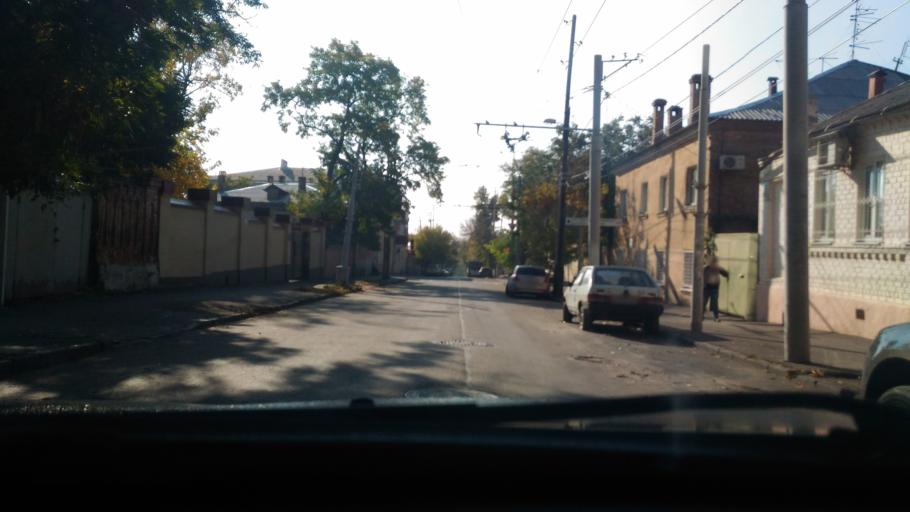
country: RU
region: Rostov
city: Rostov-na-Donu
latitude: 47.2281
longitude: 39.7631
